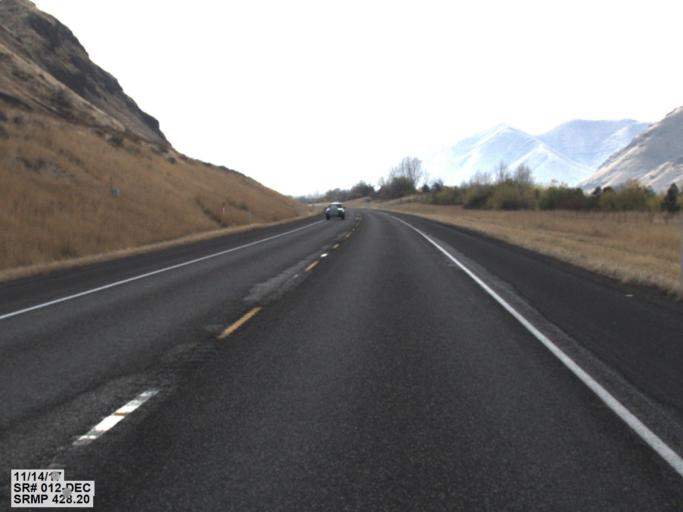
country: US
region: Washington
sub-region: Asotin County
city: Clarkston Heights-Vineland
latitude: 46.4264
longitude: -117.1555
